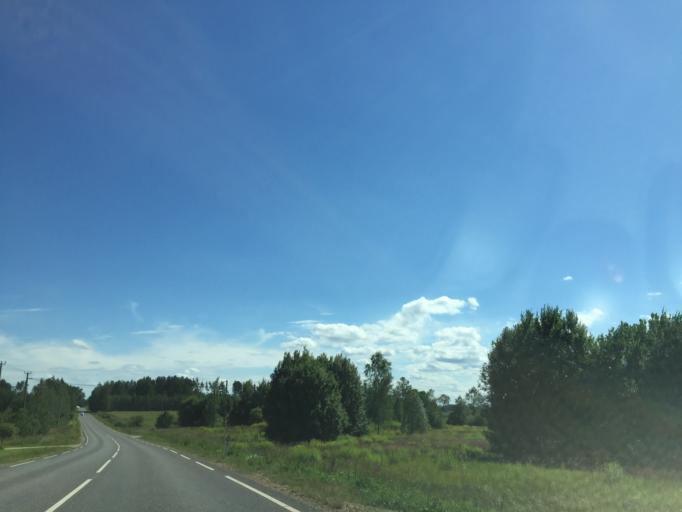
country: LV
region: Baldone
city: Baldone
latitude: 56.7351
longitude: 24.3564
